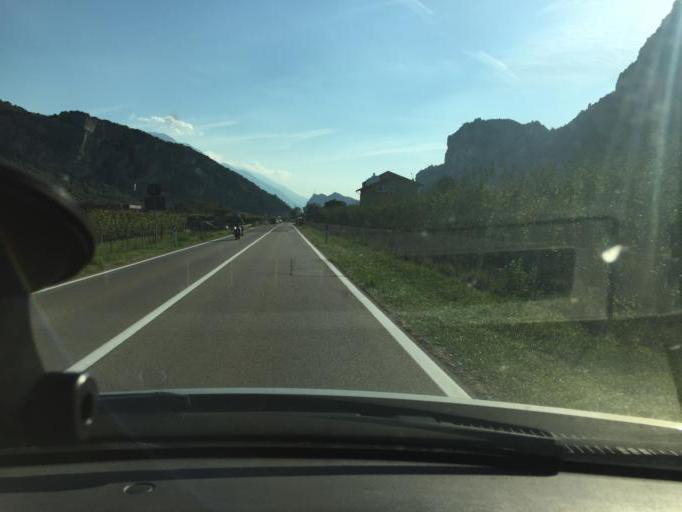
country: IT
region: Trentino-Alto Adige
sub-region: Provincia di Trento
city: Dro
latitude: 45.9438
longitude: 10.9023
